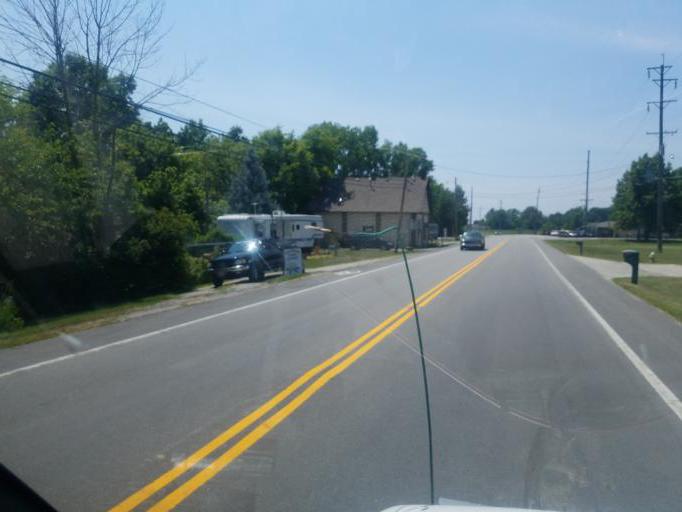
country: US
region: Ohio
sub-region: Auglaize County
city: Saint Marys
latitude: 40.5507
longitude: -84.4435
